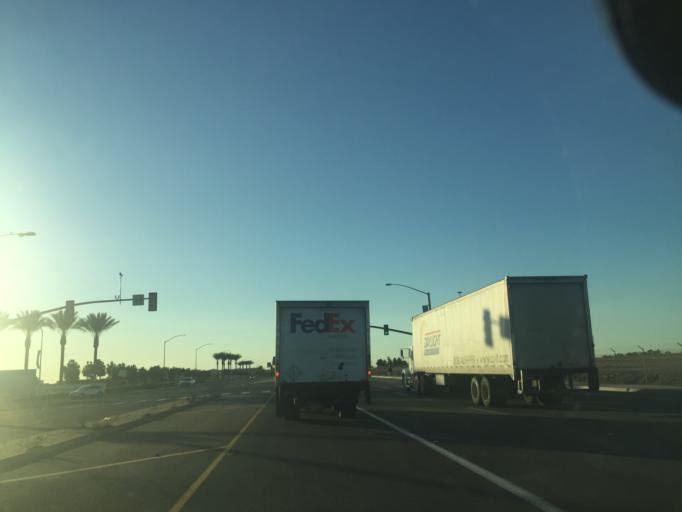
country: MX
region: Baja California
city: Tijuana
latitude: 32.5680
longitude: -116.9791
